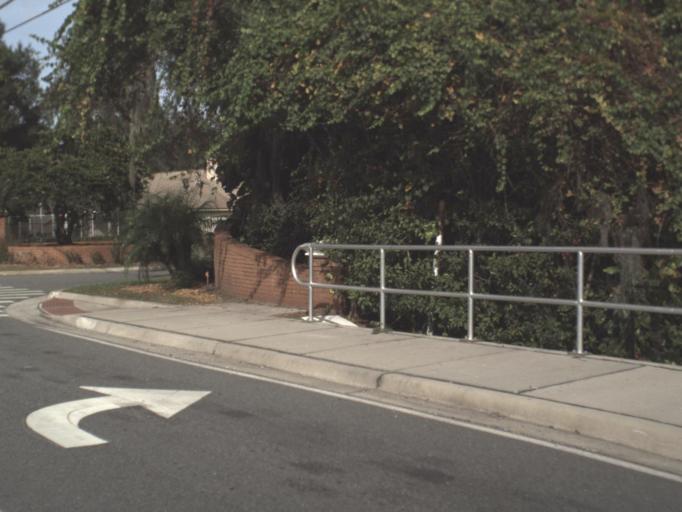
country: US
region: Florida
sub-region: Osceola County
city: Saint Cloud
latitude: 28.3421
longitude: -81.2281
